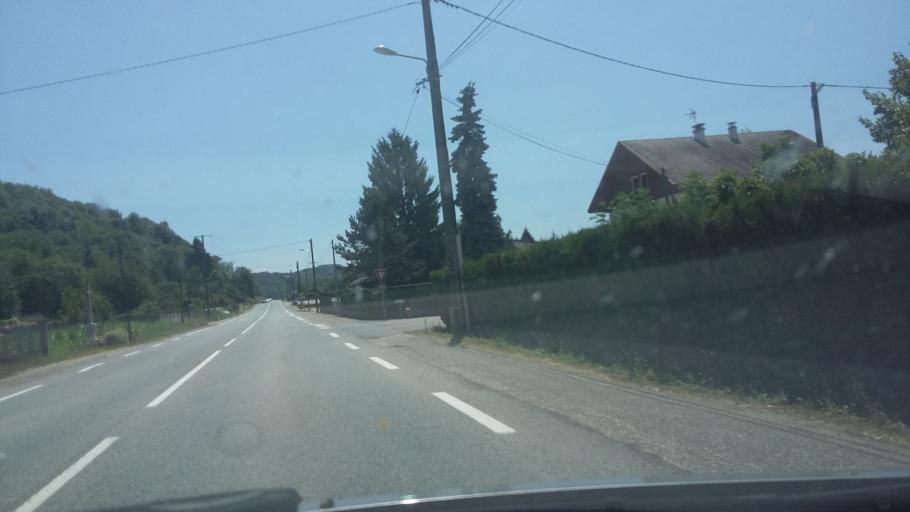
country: FR
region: Rhone-Alpes
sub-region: Departement de l'Ain
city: Belley
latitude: 45.7988
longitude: 5.6821
